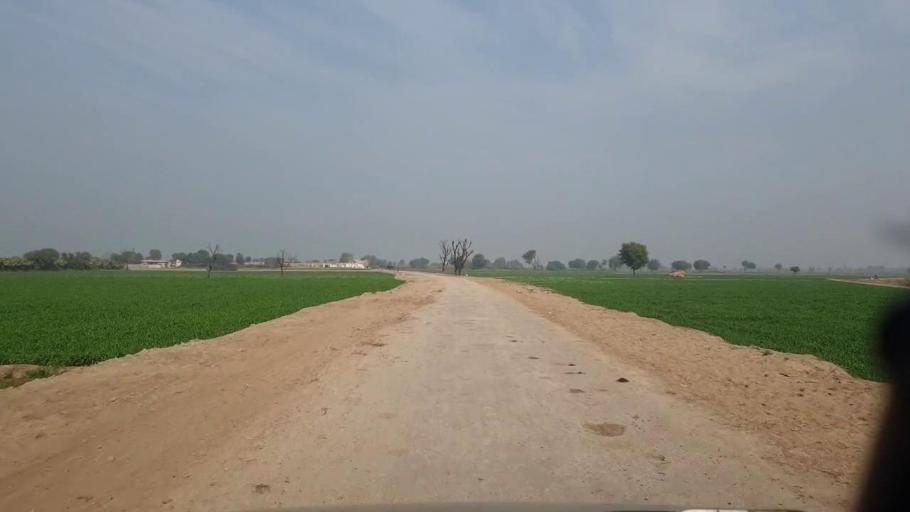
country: PK
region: Sindh
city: Shahdadpur
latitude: 26.0094
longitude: 68.5100
